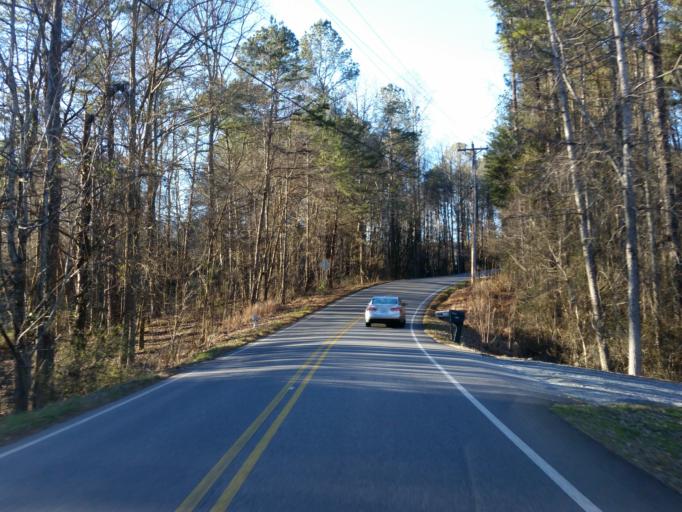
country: US
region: Georgia
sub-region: Cherokee County
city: Holly Springs
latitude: 34.1373
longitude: -84.4533
